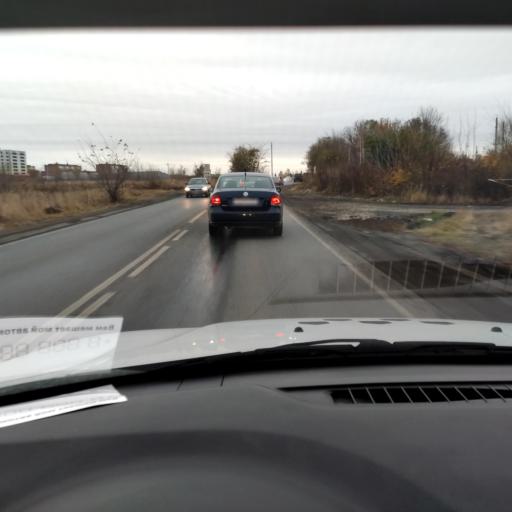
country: RU
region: Samara
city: Tol'yatti
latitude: 53.5131
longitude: 49.2453
